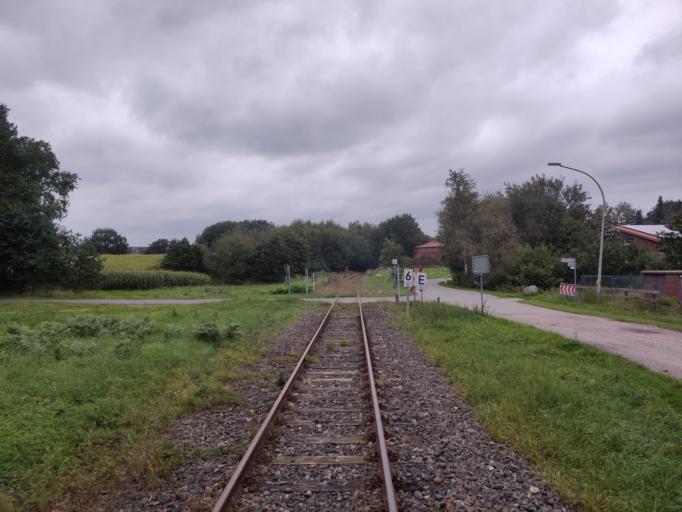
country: DE
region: Lower Saxony
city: Gnarrenburg
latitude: 53.4047
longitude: 9.0108
